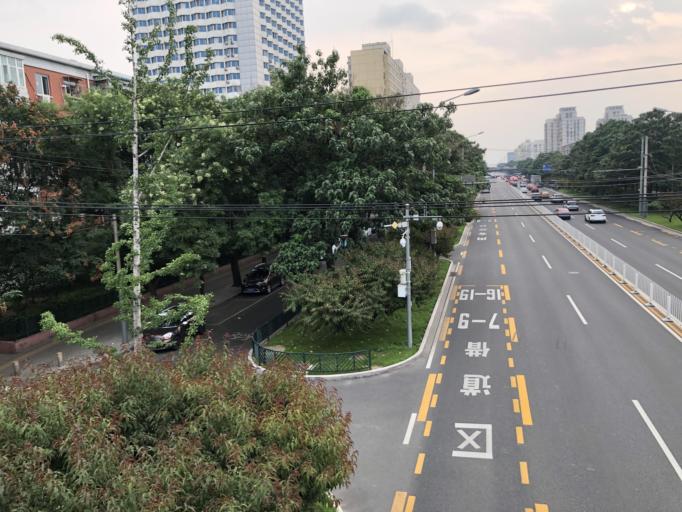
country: CN
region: Beijing
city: Sijiqing
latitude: 39.9310
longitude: 116.3092
